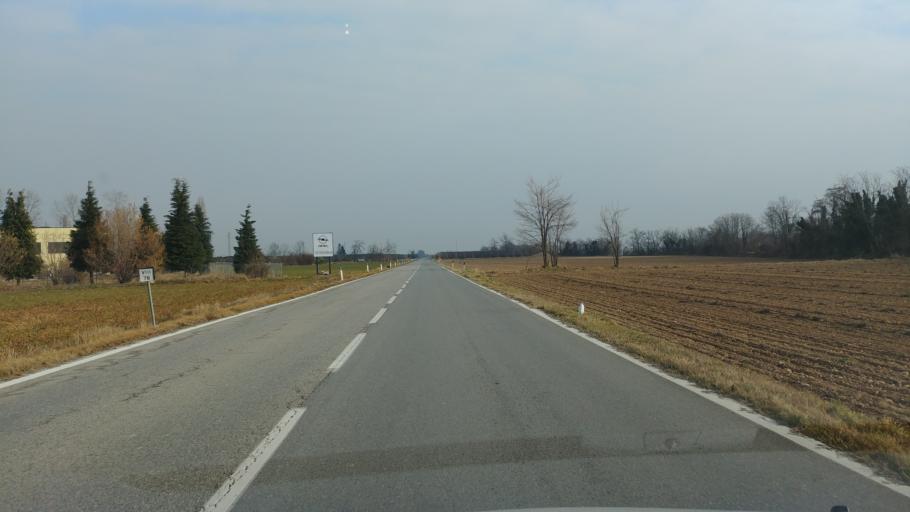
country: IT
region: Piedmont
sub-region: Provincia di Cuneo
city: Castelletto Stura
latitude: 44.4369
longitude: 7.5950
